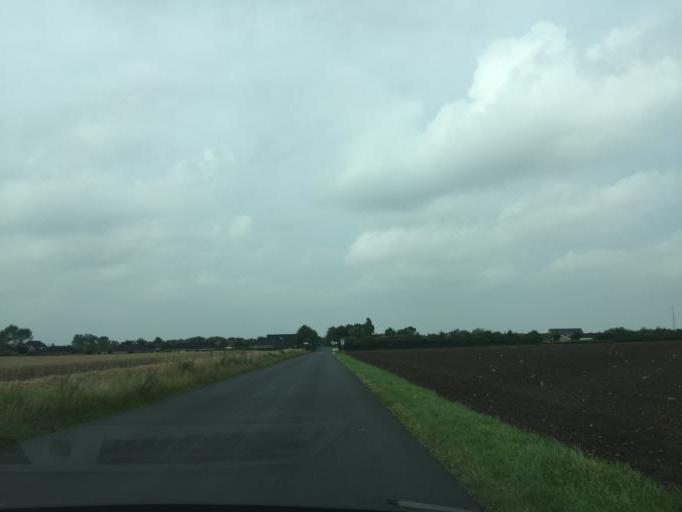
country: DK
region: South Denmark
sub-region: Odense Kommune
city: Hojby
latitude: 55.3230
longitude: 10.4280
